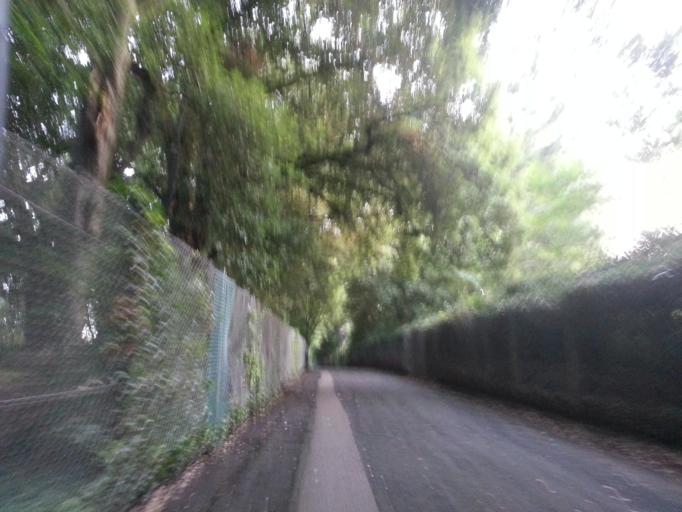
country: GB
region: England
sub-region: Suffolk
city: Ipswich
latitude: 52.0650
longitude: 1.1532
